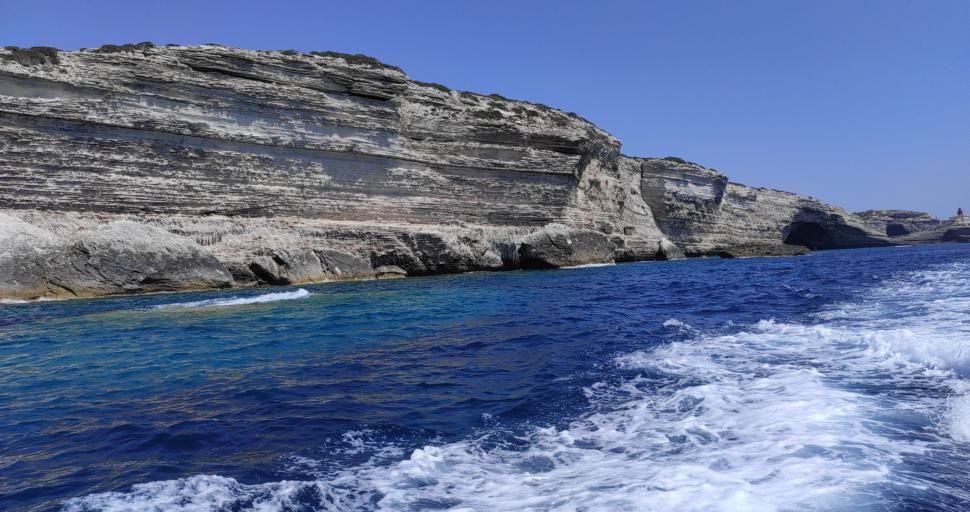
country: FR
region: Corsica
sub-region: Departement de la Corse-du-Sud
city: Bonifacio
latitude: 41.3899
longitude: 9.1372
